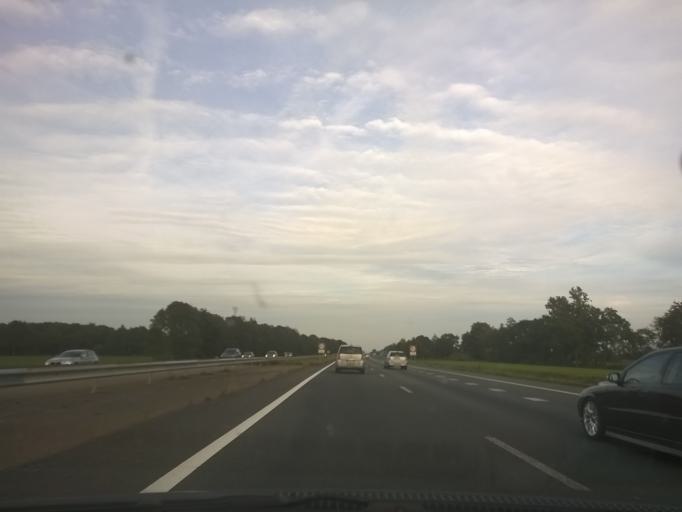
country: NL
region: Friesland
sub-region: Gemeente Smallingerland
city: Drachtstercompagnie
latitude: 53.1330
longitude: 6.1955
